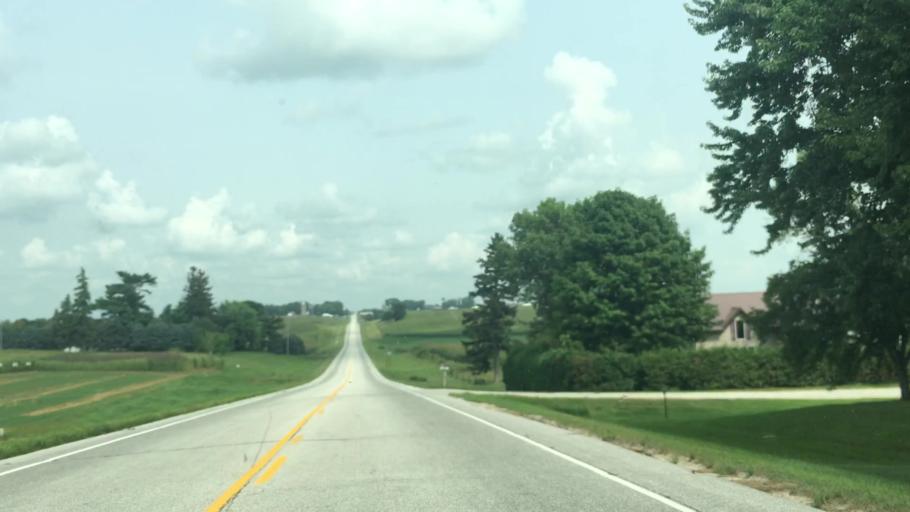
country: US
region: Minnesota
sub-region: Fillmore County
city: Harmony
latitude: 43.6023
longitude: -91.9297
